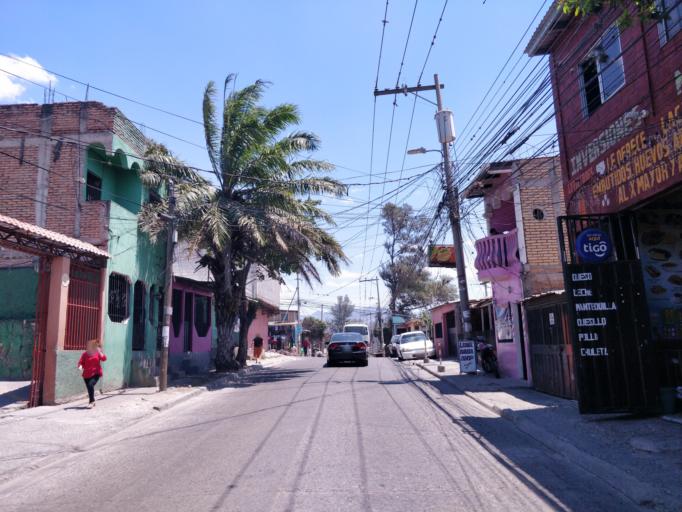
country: HN
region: Francisco Morazan
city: Tegucigalpa
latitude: 14.0959
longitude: -87.2159
